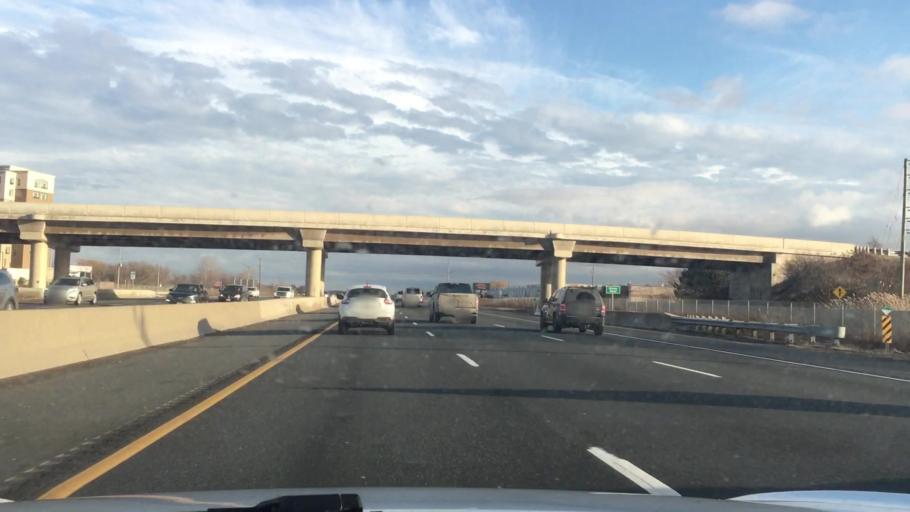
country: CA
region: Ontario
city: Hamilton
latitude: 43.2368
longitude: -79.7192
